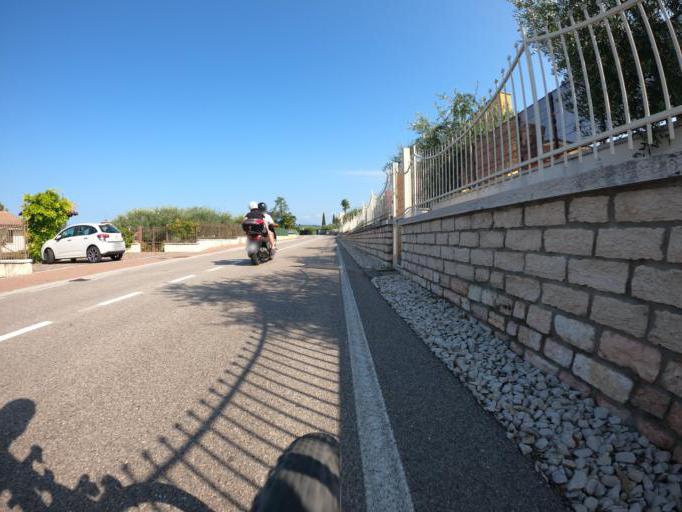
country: IT
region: Veneto
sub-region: Provincia di Verona
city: Bardolino
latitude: 45.5386
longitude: 10.7346
